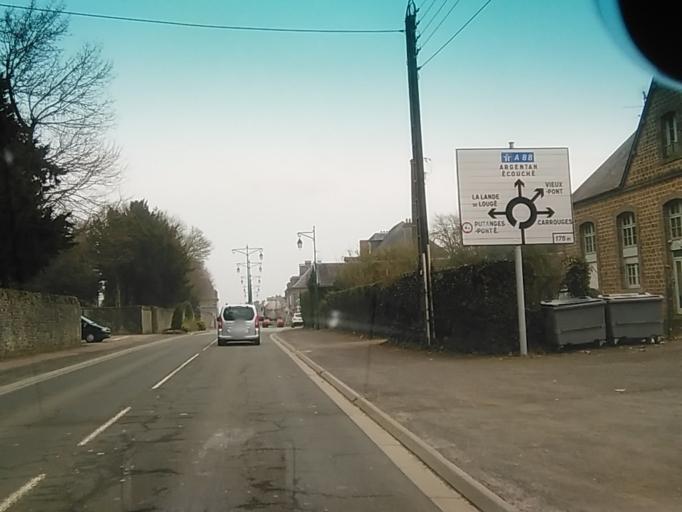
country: FR
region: Lower Normandy
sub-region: Departement de l'Orne
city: Ecouche
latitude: 48.6394
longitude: -0.2132
